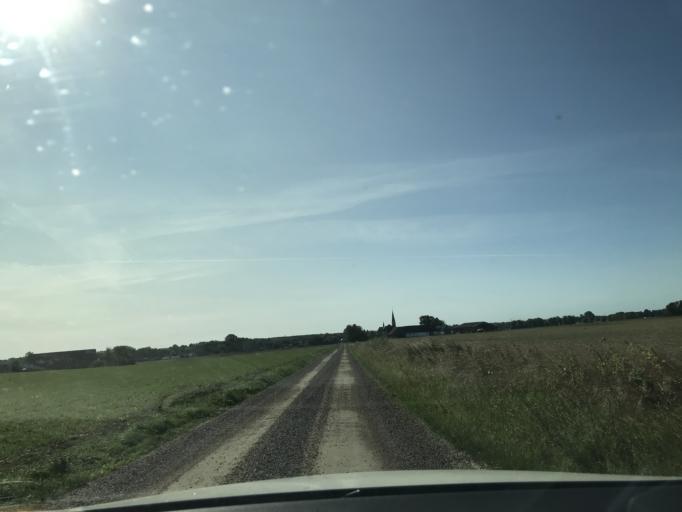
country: SE
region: Skane
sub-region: Landskrona
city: Asmundtorp
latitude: 55.8980
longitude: 12.9490
